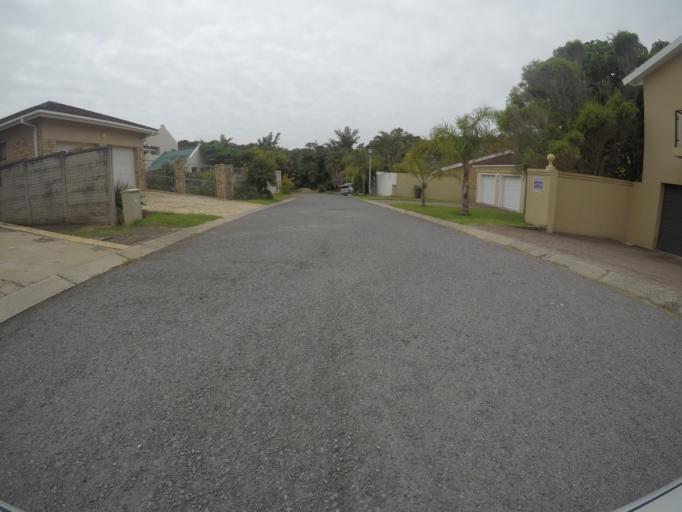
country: ZA
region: Eastern Cape
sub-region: Buffalo City Metropolitan Municipality
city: East London
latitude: -32.9767
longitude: 27.9542
